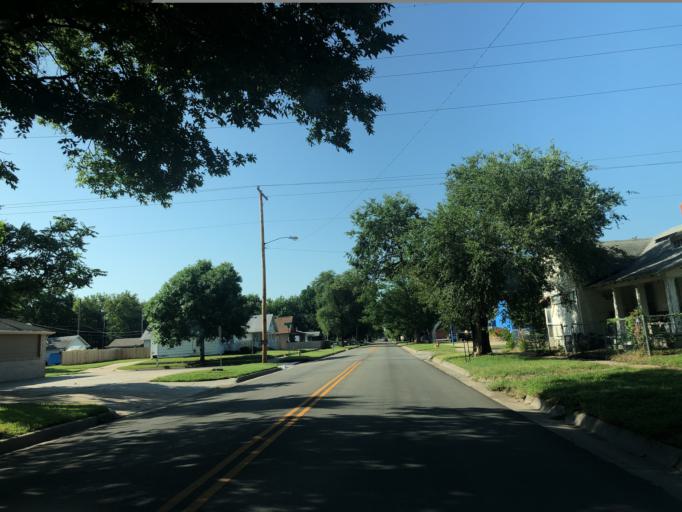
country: US
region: Kansas
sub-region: Sedgwick County
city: Wichita
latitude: 37.7287
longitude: -97.3448
